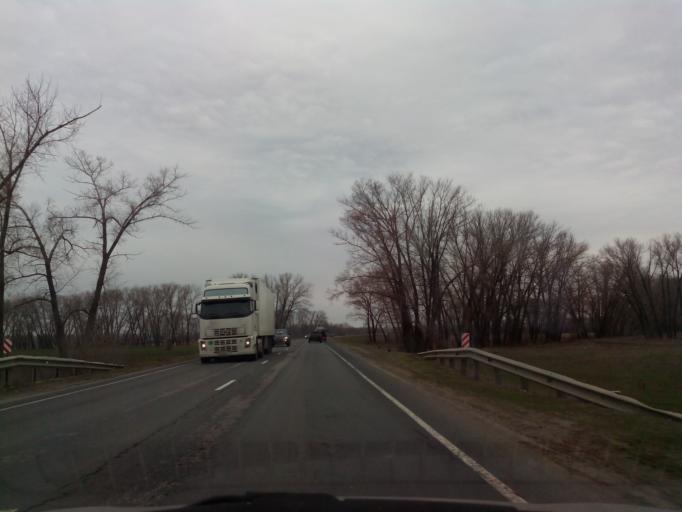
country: RU
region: Tambov
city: Zavoronezhskoye
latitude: 52.9492
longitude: 40.5858
